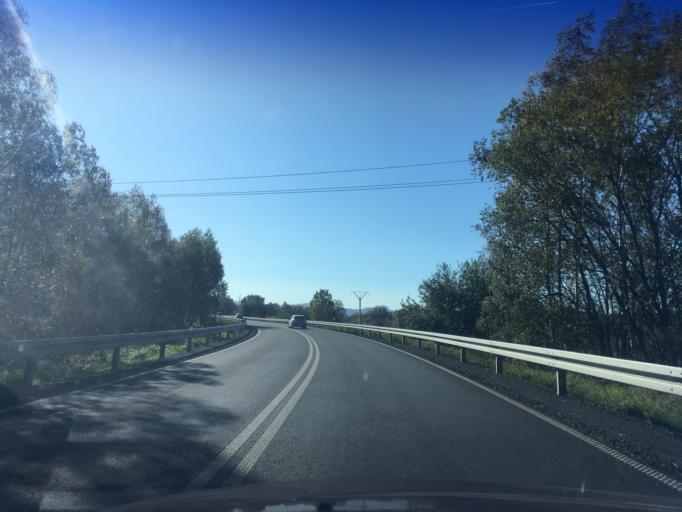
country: DE
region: Saxony
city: Hirschfelde
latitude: 50.9310
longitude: 14.8766
